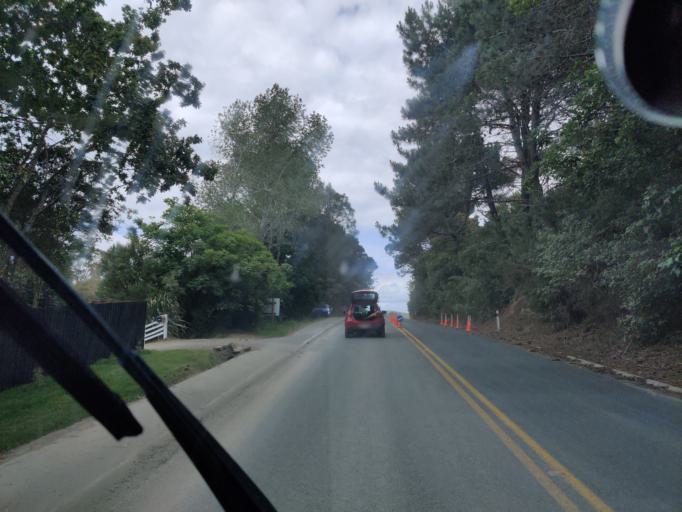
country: NZ
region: Northland
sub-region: Far North District
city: Taipa
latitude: -34.9932
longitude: 173.4751
